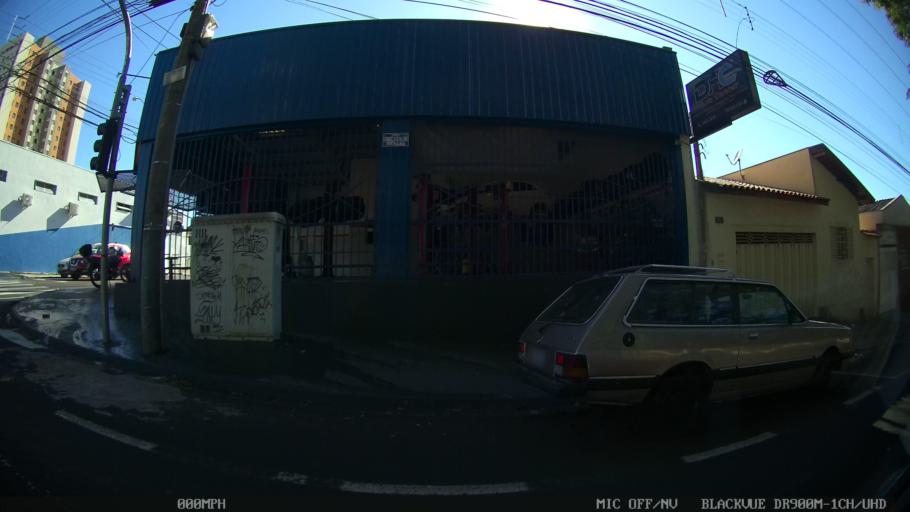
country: BR
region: Sao Paulo
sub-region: Franca
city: Franca
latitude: -20.5306
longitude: -47.4050
